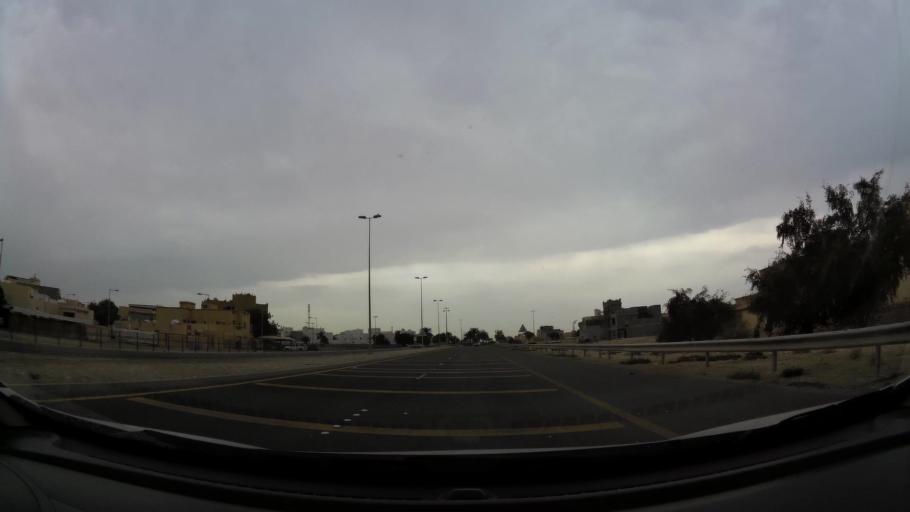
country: BH
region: Central Governorate
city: Madinat Hamad
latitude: 26.1050
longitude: 50.4977
